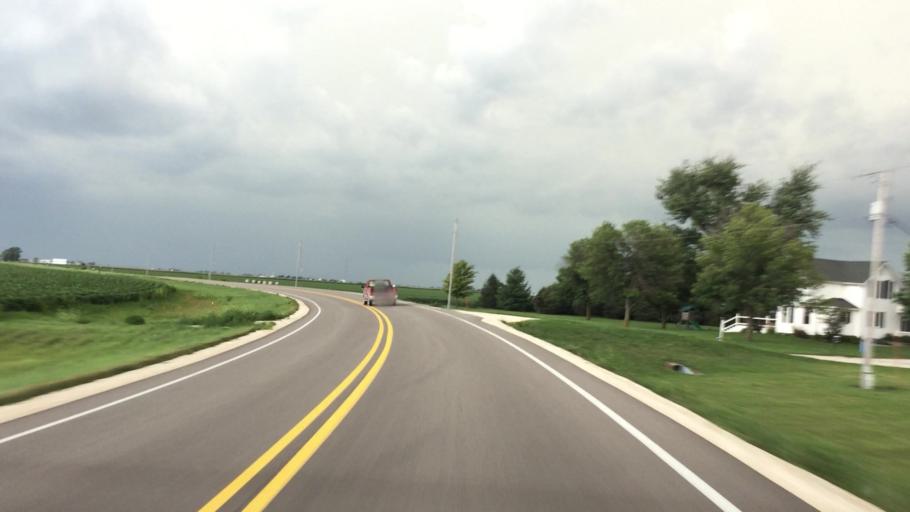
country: US
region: Iowa
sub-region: Henry County
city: New London
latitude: 40.7838
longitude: -91.4799
